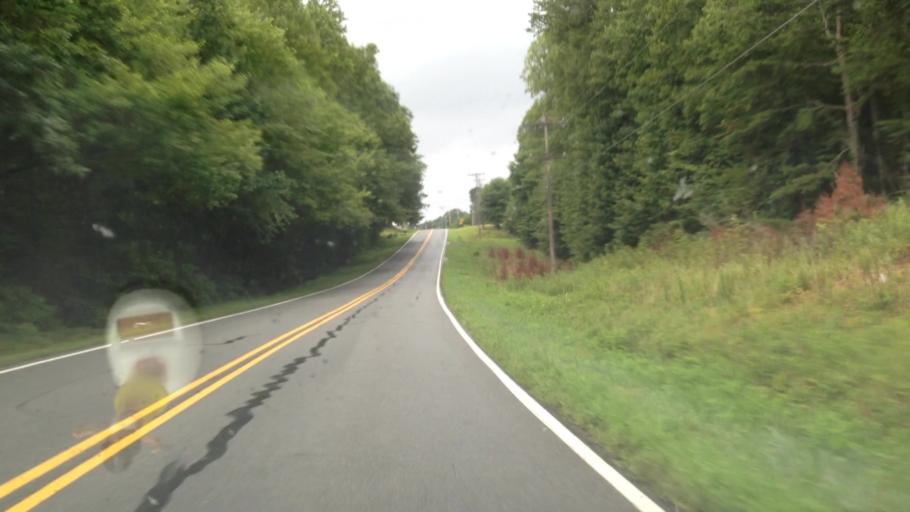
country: US
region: North Carolina
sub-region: Stokes County
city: Walnut Cove
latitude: 36.2805
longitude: -80.0806
